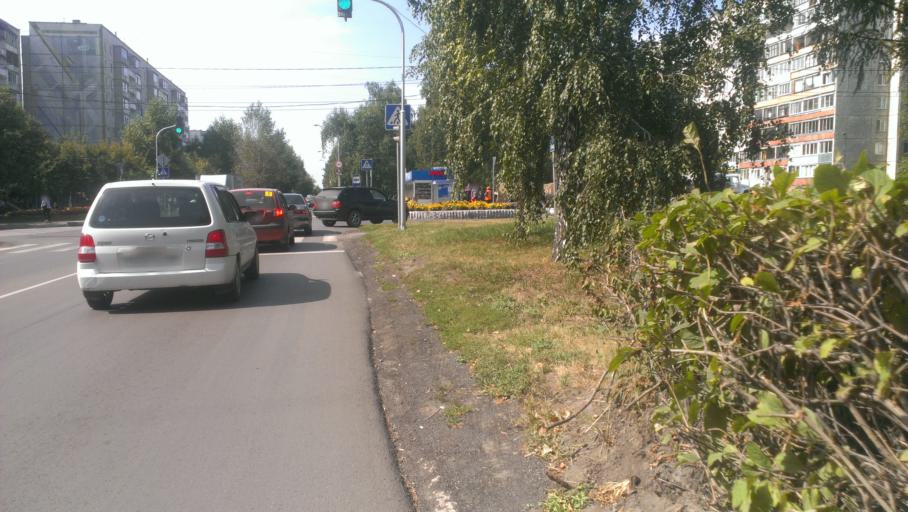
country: RU
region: Altai Krai
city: Novosilikatnyy
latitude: 53.3673
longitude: 83.6692
